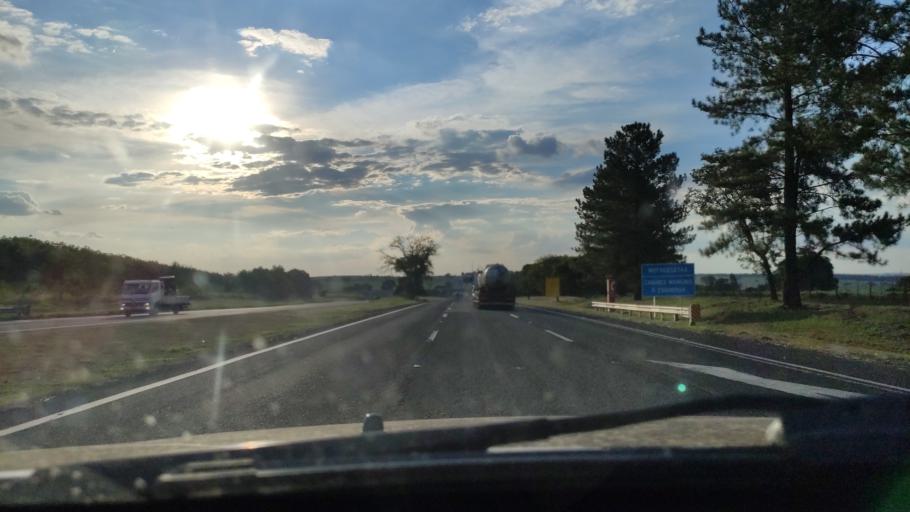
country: BR
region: Sao Paulo
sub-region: Rancharia
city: Rancharia
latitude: -22.4444
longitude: -50.9927
